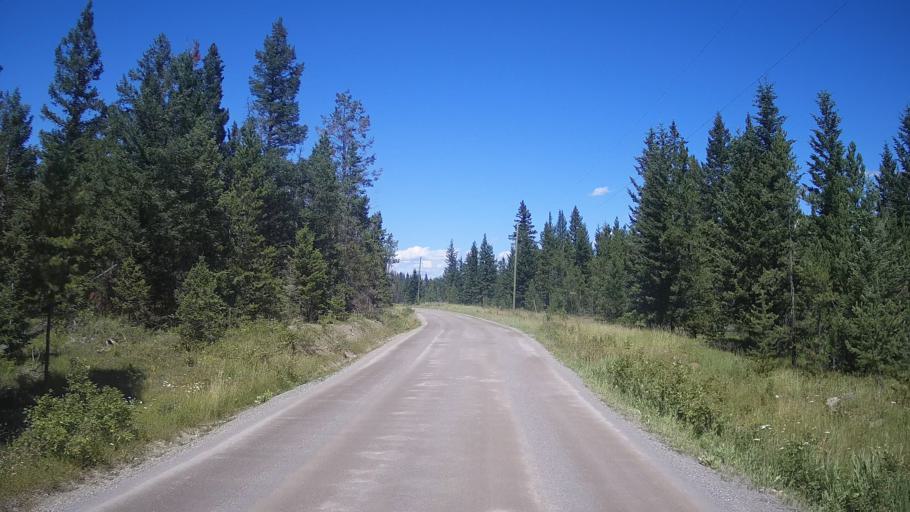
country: CA
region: British Columbia
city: Cache Creek
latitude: 51.1979
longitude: -121.5907
